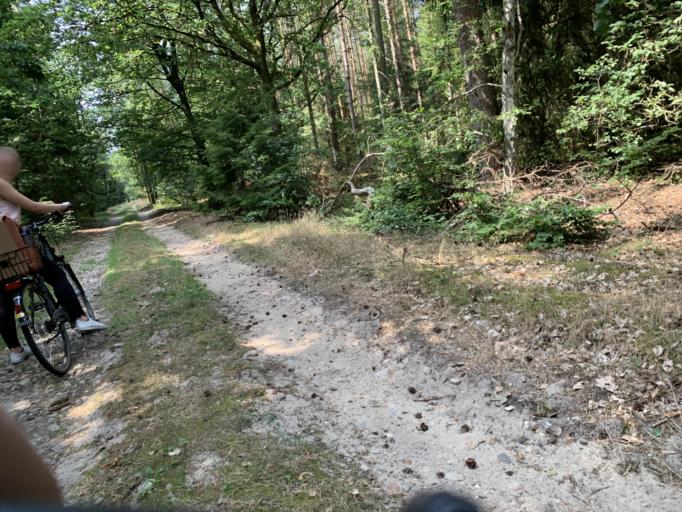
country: DE
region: Lower Saxony
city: Thomasburg
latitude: 53.2017
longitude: 10.6770
